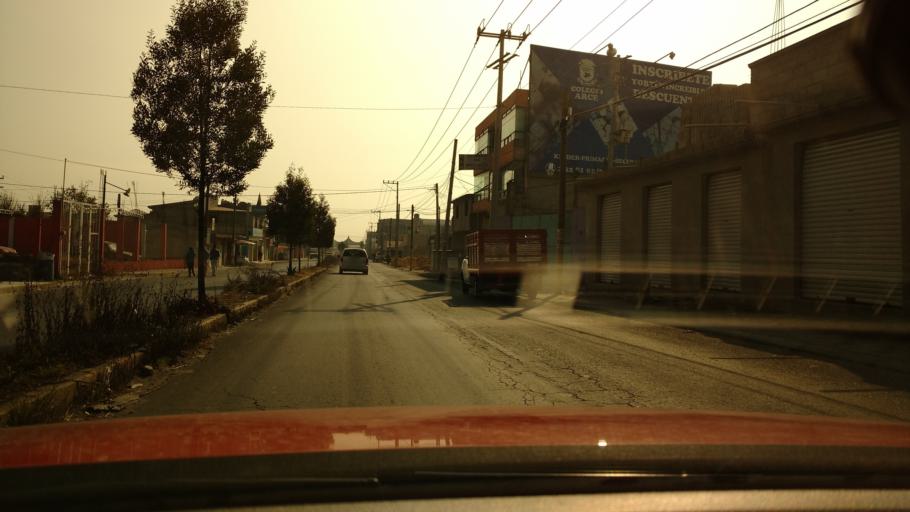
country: MX
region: Mexico
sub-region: Calimaya
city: Colonia Arboledas (San Andres)
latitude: 19.2055
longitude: -99.5754
